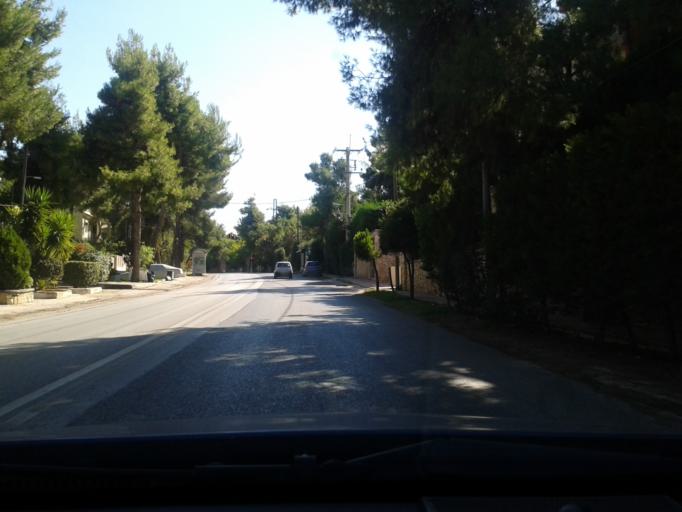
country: GR
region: Attica
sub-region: Nomarchia Anatolikis Attikis
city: Drosia
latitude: 38.1068
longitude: 23.8639
